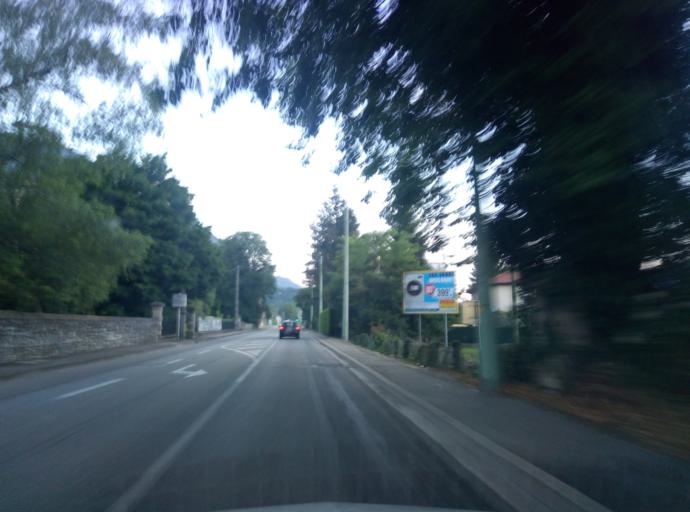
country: FR
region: Rhone-Alpes
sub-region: Departement de l'Isere
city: Sassenage
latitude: 45.2025
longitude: 5.6669
